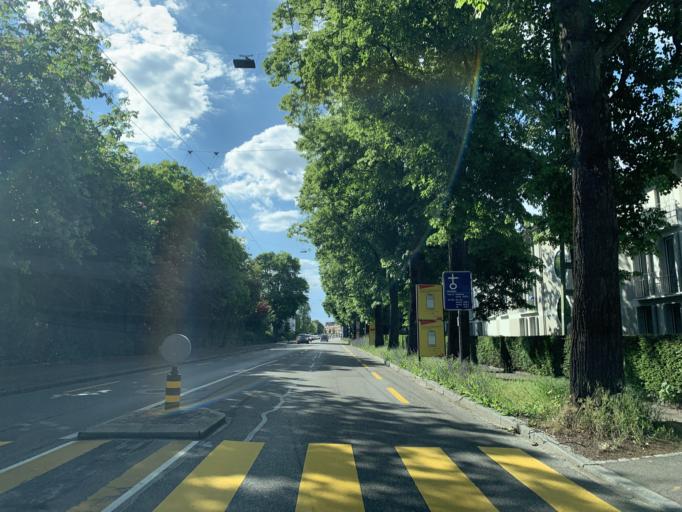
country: CH
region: Zurich
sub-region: Bezirk Winterthur
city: Mattenbach (Kreis 7)
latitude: 47.4916
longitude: 8.7460
